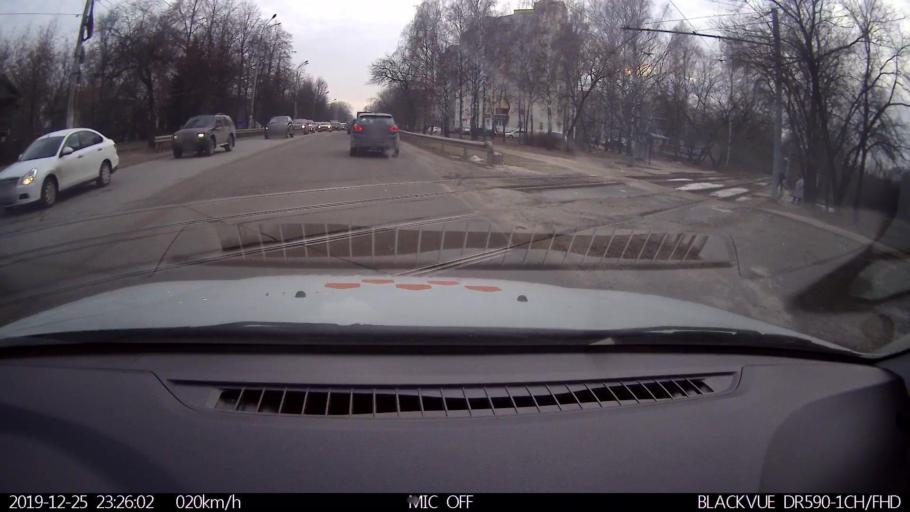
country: RU
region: Nizjnij Novgorod
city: Gorbatovka
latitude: 56.3480
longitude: 43.8373
